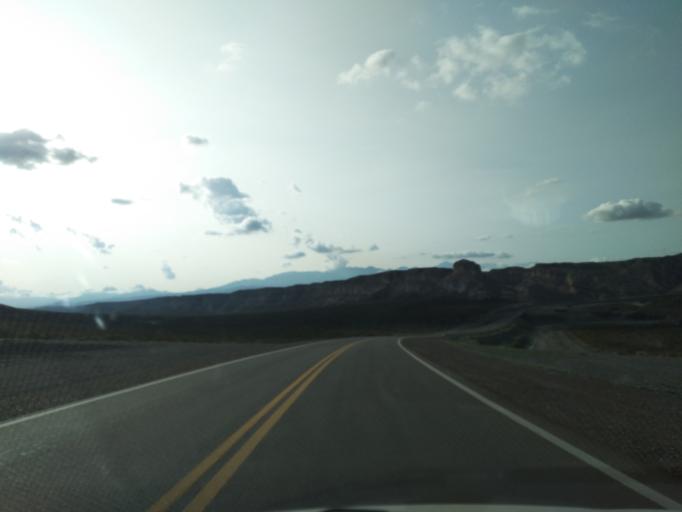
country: AR
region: Mendoza
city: San Rafael
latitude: -34.6436
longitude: -69.1746
